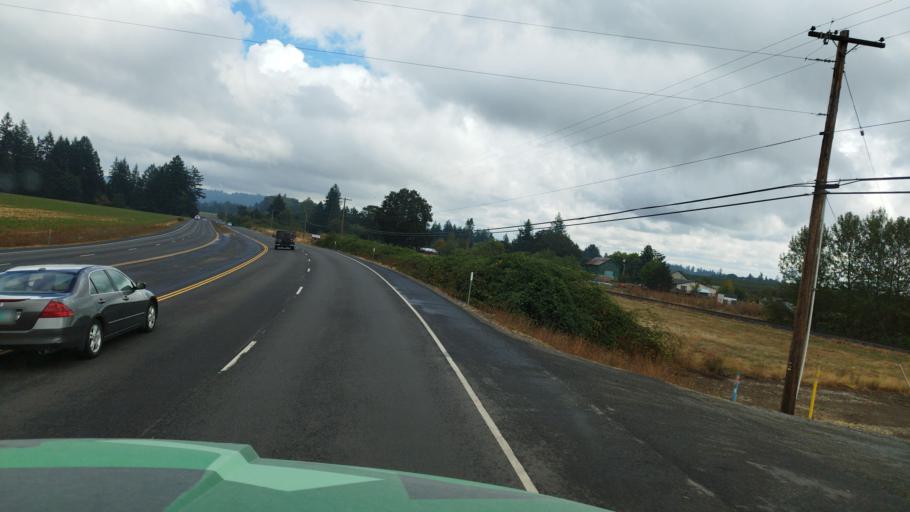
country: US
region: Oregon
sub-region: Yamhill County
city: Lafayette
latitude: 45.2399
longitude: -123.1412
